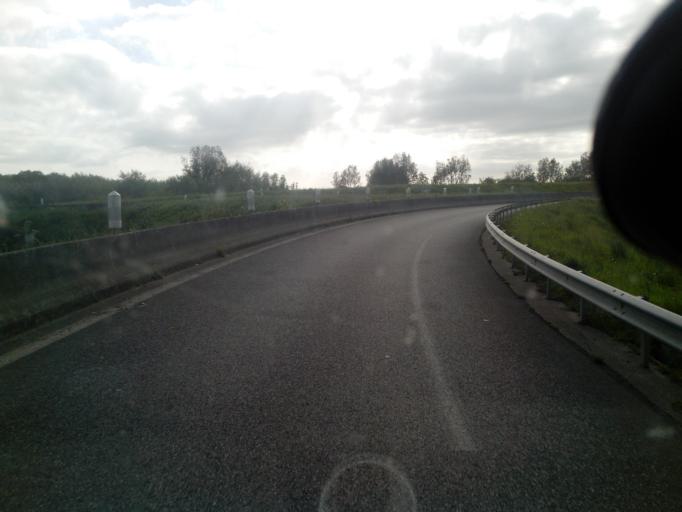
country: FR
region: Haute-Normandie
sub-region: Departement de l'Eure
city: Beuzeville
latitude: 49.3182
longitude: 0.3164
